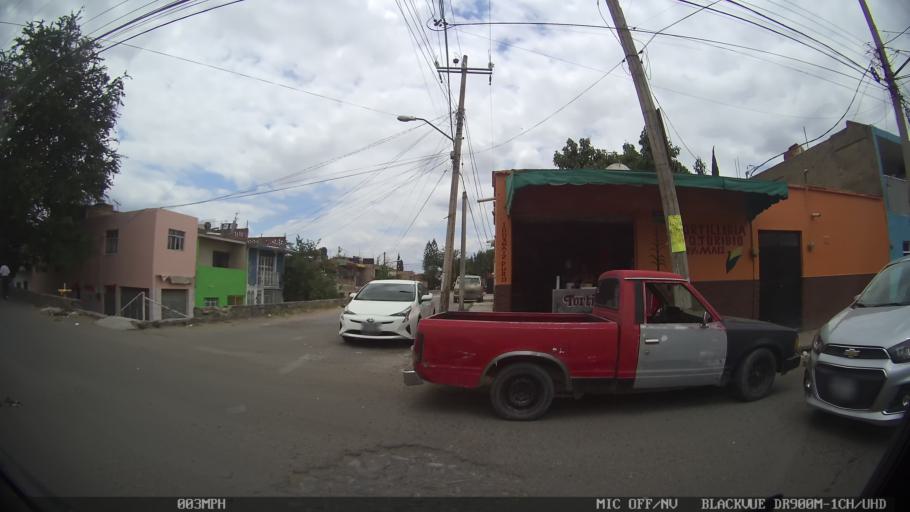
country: MX
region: Jalisco
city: Tlaquepaque
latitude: 20.6525
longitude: -103.2586
